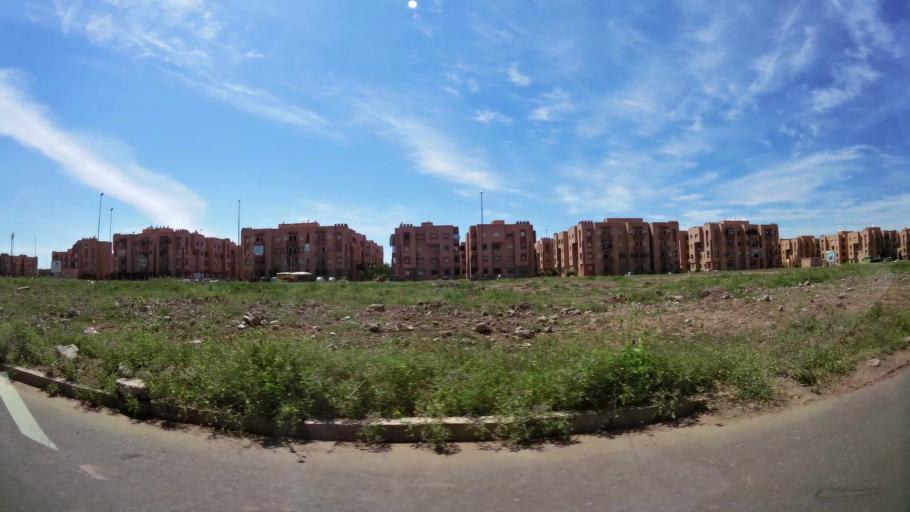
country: MA
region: Marrakech-Tensift-Al Haouz
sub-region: Marrakech
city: Marrakesh
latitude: 31.6460
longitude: -8.0790
